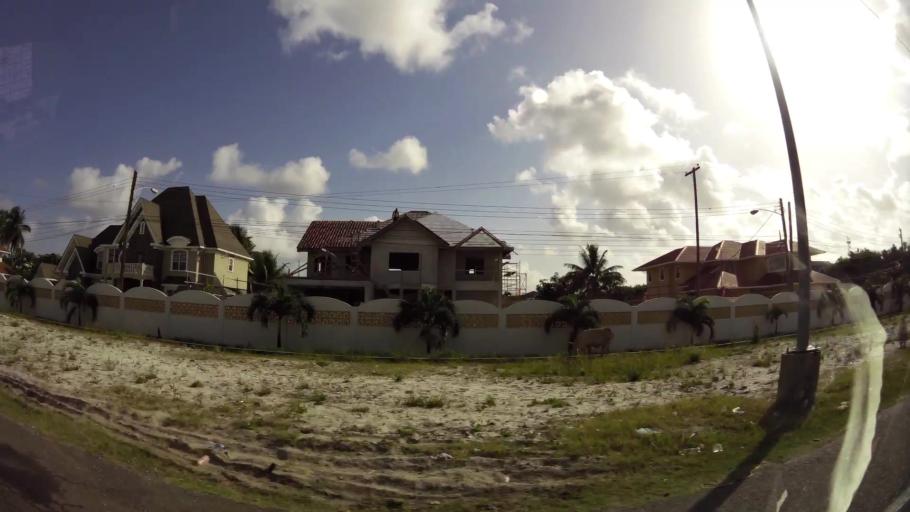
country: GY
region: Demerara-Mahaica
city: Georgetown
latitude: 6.8167
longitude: -58.0750
